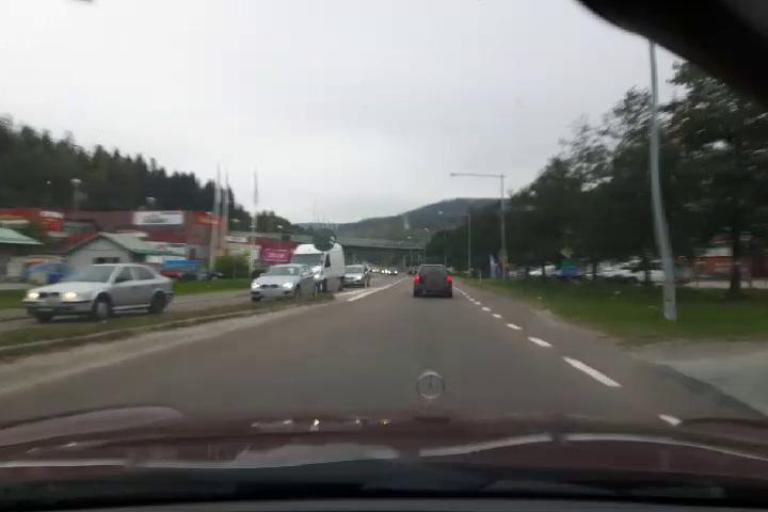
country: SE
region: Vaesternorrland
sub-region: OErnskoeldsviks Kommun
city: Ornskoldsvik
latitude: 63.2920
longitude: 18.7021
